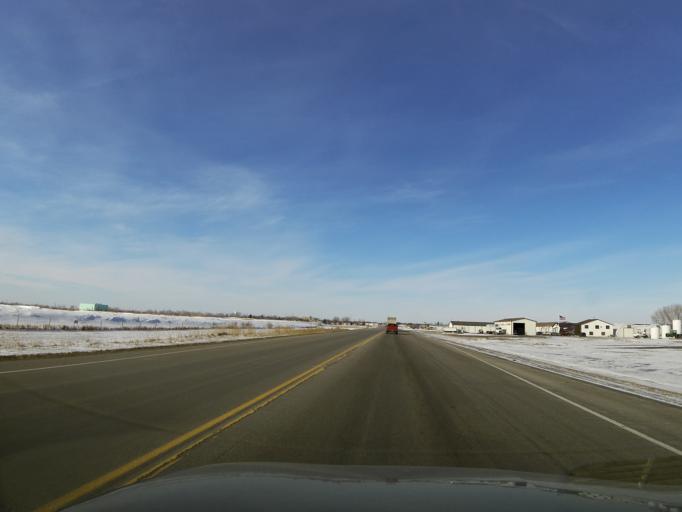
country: US
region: North Dakota
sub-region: Walsh County
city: Grafton
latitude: 48.4126
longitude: -97.3826
